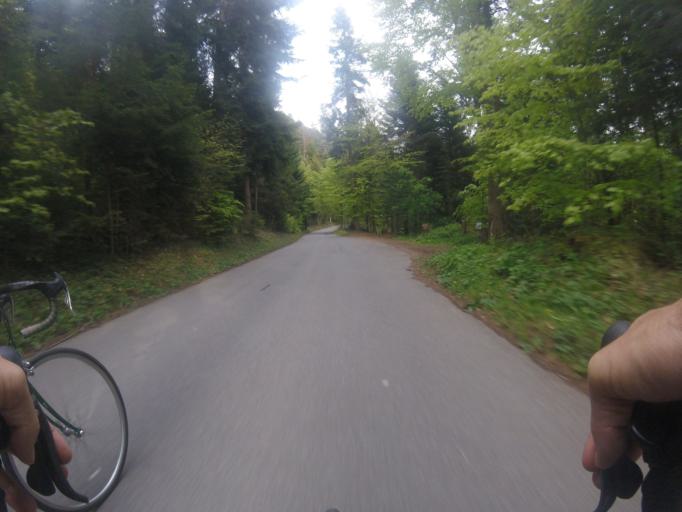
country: CH
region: Lucerne
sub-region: Entlebuch District
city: Oberdiessbach
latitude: 46.8364
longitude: 7.6030
